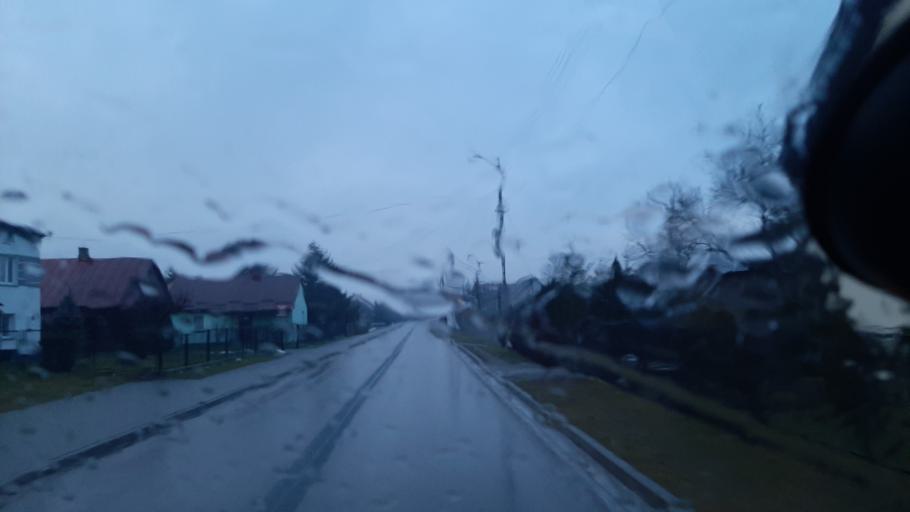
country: PL
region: Lublin Voivodeship
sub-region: Powiat lubartowski
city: Firlej
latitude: 51.5444
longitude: 22.5651
